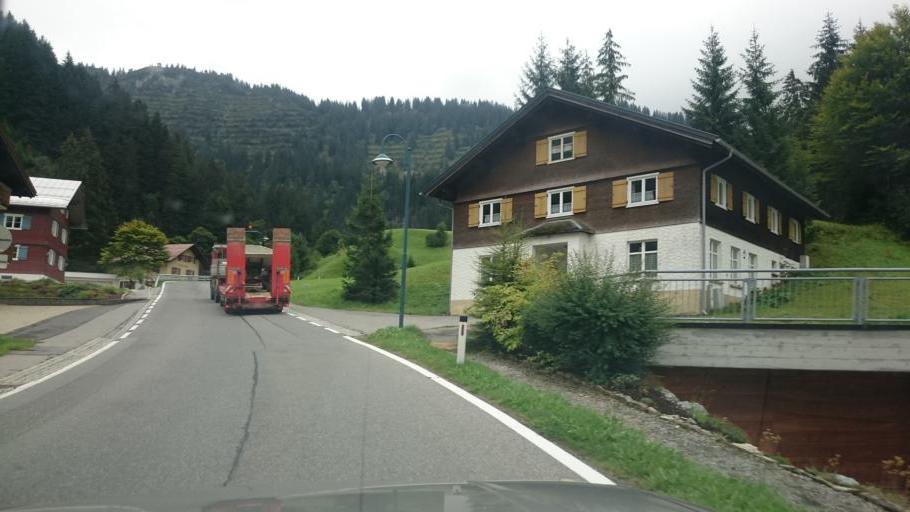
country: AT
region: Vorarlberg
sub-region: Politischer Bezirk Bregenz
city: Schroecken
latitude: 47.2596
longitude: 10.0892
